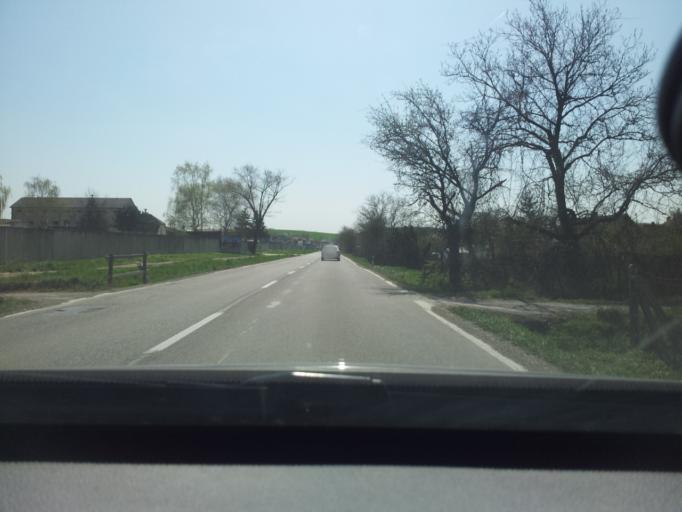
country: SK
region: Nitriansky
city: Banovce nad Bebravou
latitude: 48.7851
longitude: 18.1717
